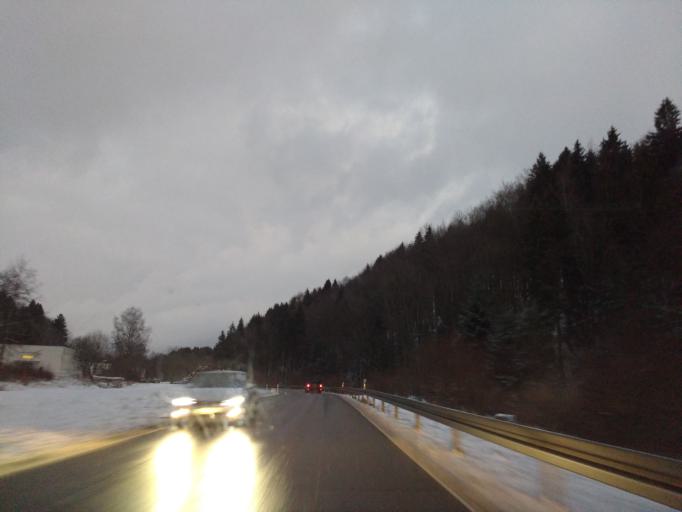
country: DE
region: Bavaria
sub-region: Swabia
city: Buchenberg
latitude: 47.7084
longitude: 10.2644
